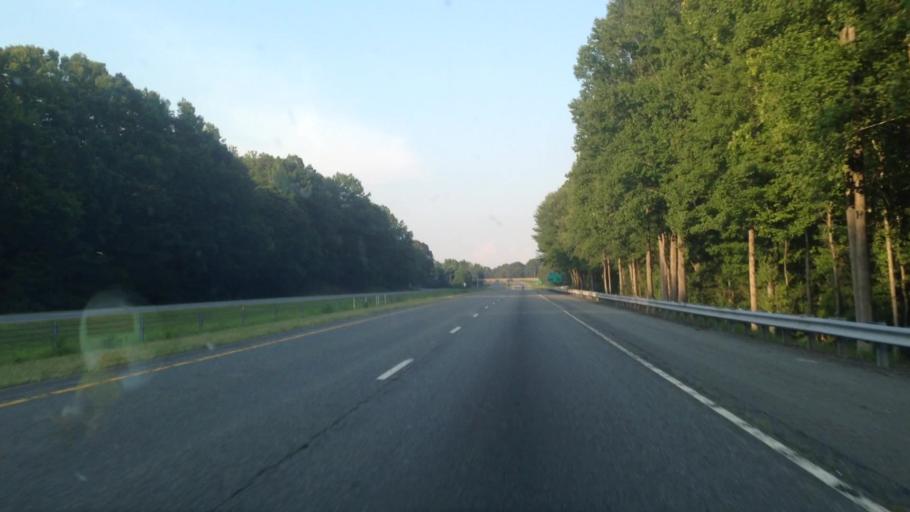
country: US
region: North Carolina
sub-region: Rockingham County
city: Reidsville
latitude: 36.4527
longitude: -79.5512
